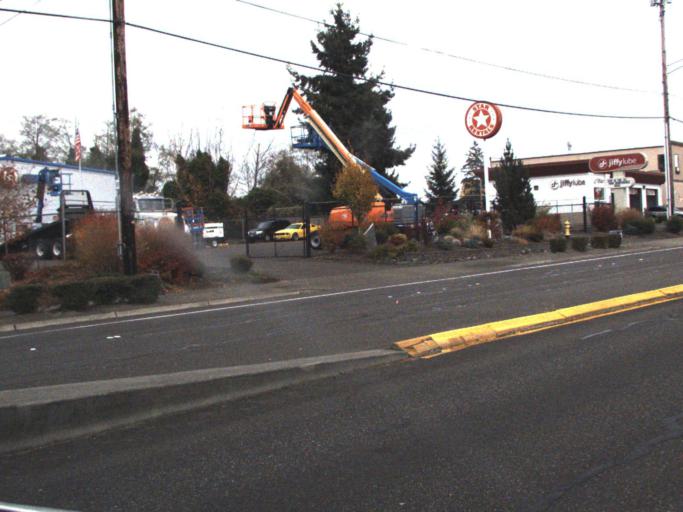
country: US
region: Washington
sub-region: Snohomish County
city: Martha Lake
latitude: 47.8850
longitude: -122.2817
